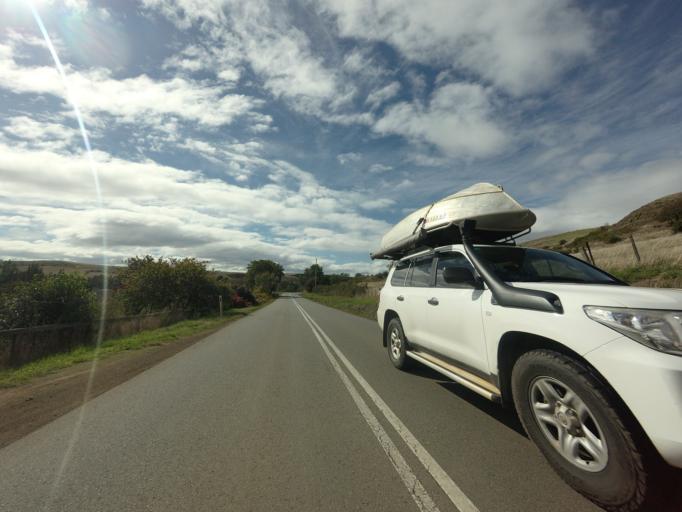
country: AU
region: Tasmania
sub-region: Derwent Valley
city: New Norfolk
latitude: -42.7067
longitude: 146.9131
